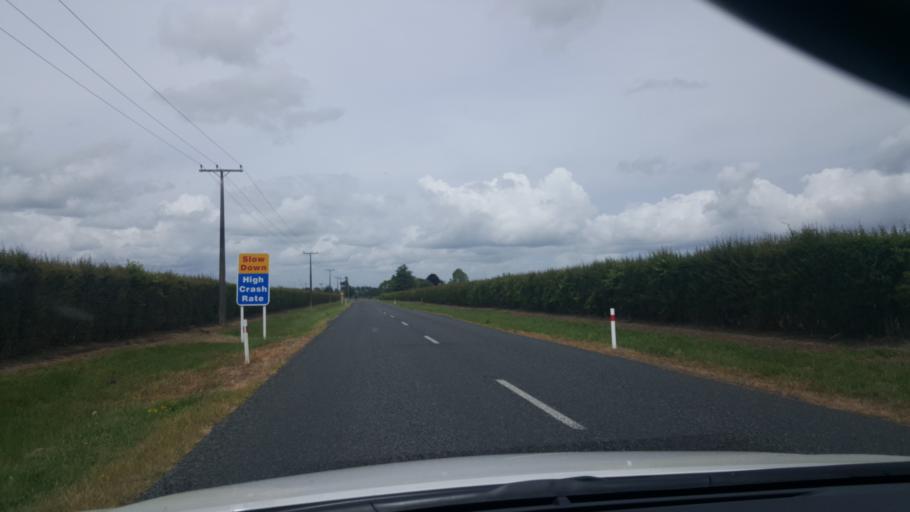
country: NZ
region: Waikato
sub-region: Matamata-Piako District
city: Matamata
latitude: -37.8802
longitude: 175.7300
